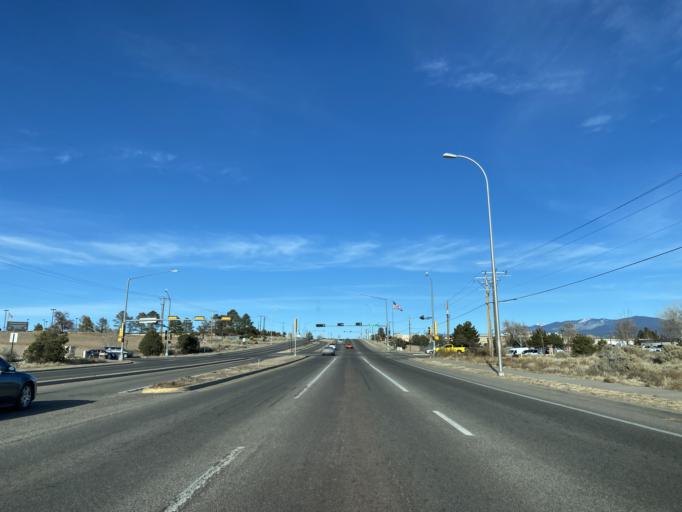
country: US
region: New Mexico
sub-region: Santa Fe County
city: Agua Fria
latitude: 35.6270
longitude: -106.0246
